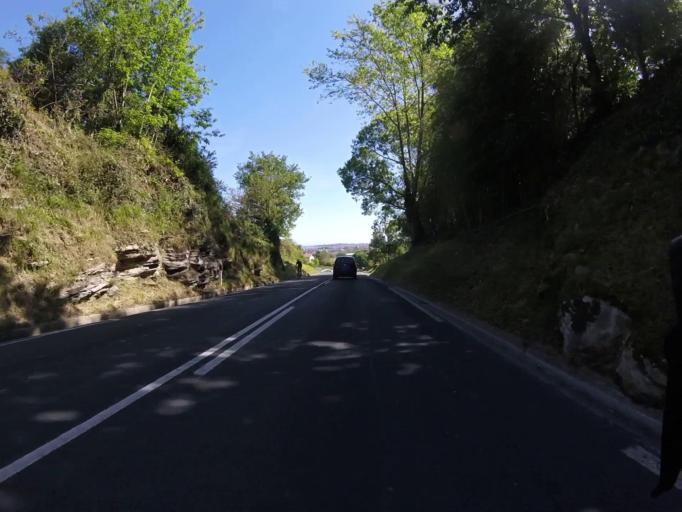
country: ES
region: Basque Country
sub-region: Provincia de Guipuzcoa
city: Irun
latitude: 43.3217
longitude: -1.8282
